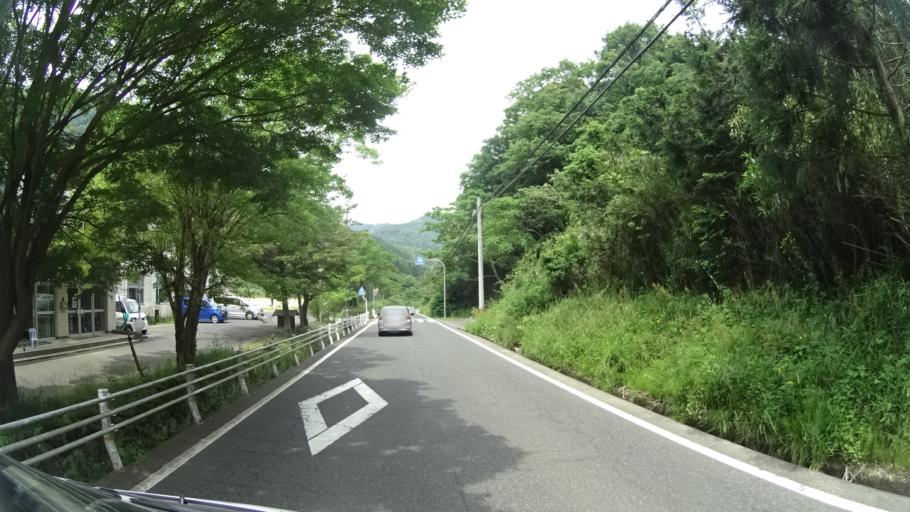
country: JP
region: Kyoto
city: Miyazu
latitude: 35.6877
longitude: 135.2819
